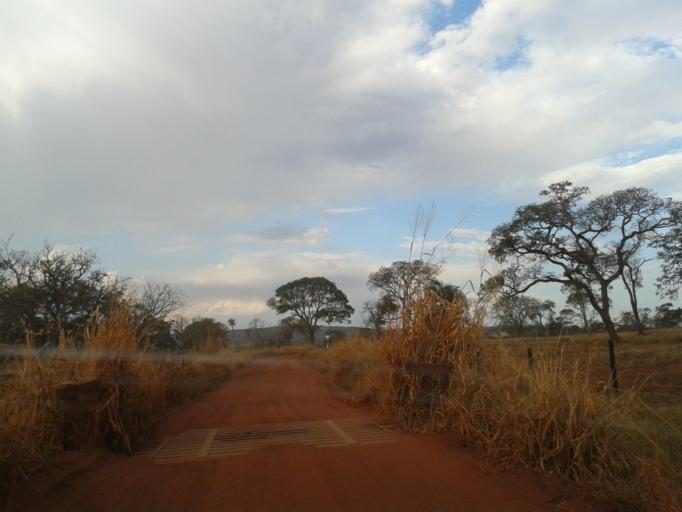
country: BR
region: Minas Gerais
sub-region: Ituiutaba
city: Ituiutaba
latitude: -19.1987
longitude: -49.8360
